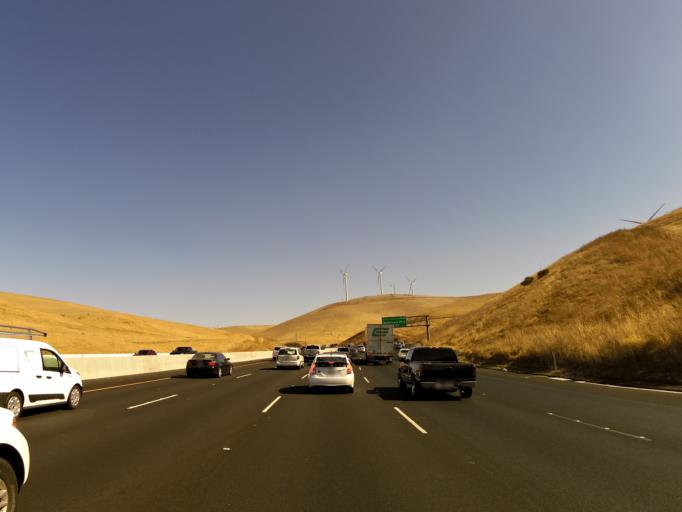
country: US
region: California
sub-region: Alameda County
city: Livermore
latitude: 37.7207
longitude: -121.6743
